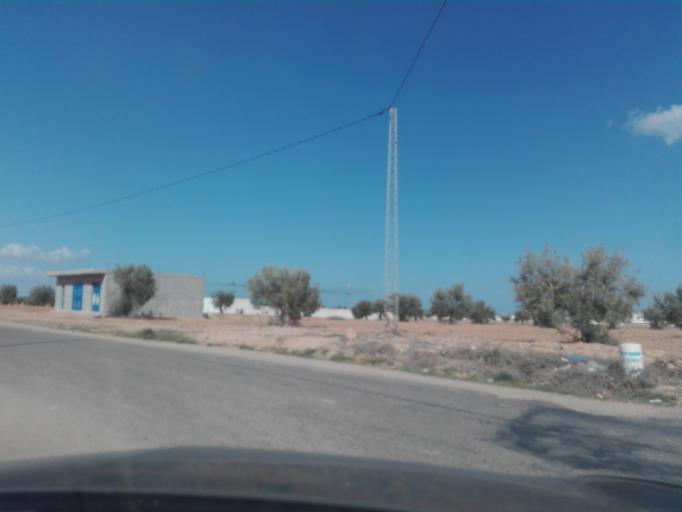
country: TN
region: Madanin
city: Bin Qirdan
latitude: 33.1695
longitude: 11.1971
